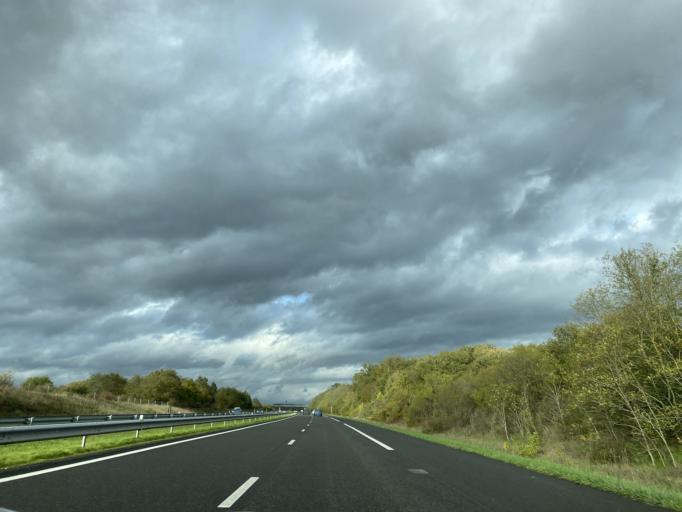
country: FR
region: Centre
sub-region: Departement du Cher
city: Orval
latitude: 46.7964
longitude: 2.4136
